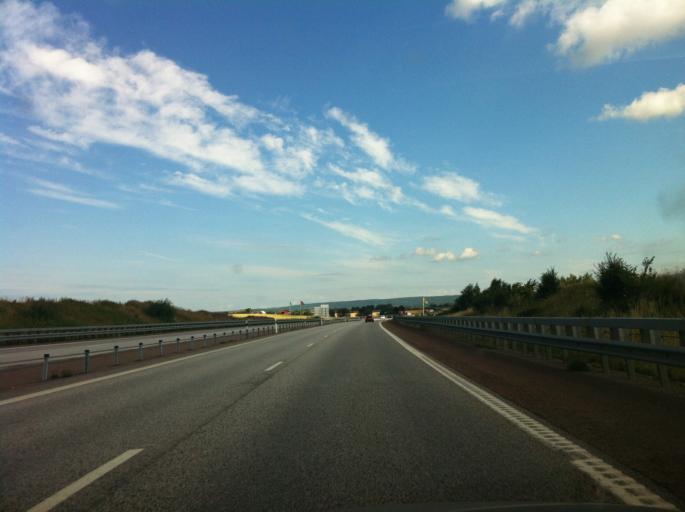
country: SE
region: Skane
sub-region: Angelholms Kommun
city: AEngelholm
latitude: 56.2623
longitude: 12.8949
